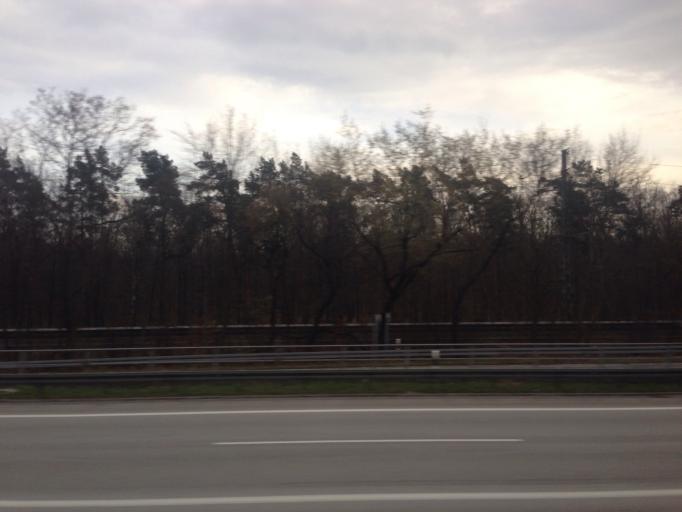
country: DE
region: Berlin
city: Grunewald
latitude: 52.4684
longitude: 13.2356
